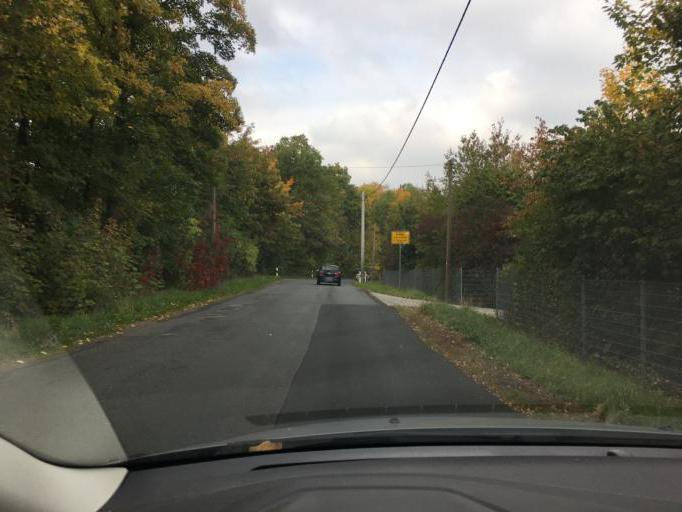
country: DE
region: Saxony
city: Freital
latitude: 50.9942
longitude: 13.6756
